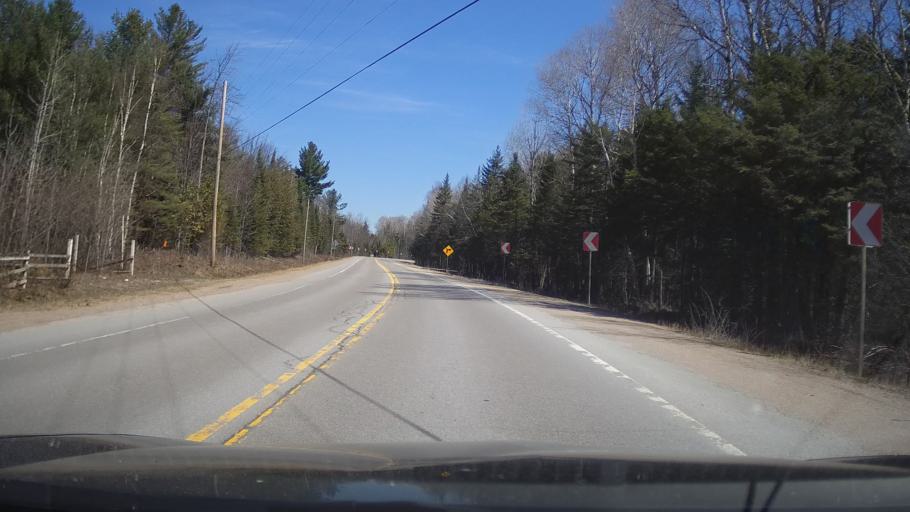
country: CA
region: Ontario
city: Arnprior
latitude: 45.5463
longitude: -76.3627
